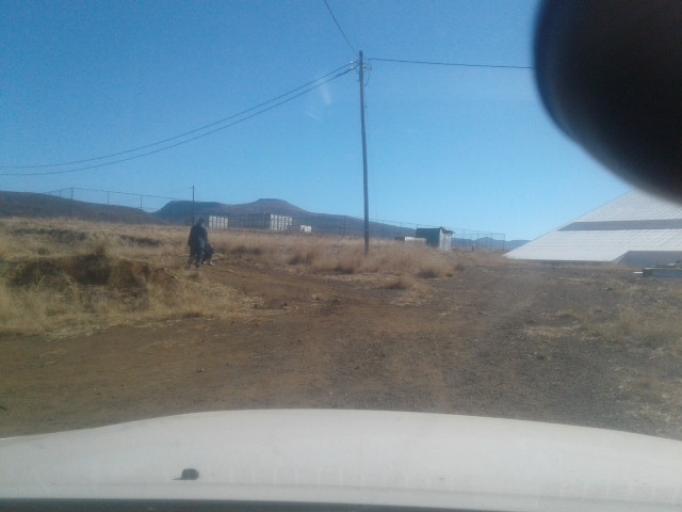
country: LS
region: Berea
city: Teyateyaneng
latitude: -29.3714
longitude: 28.0347
